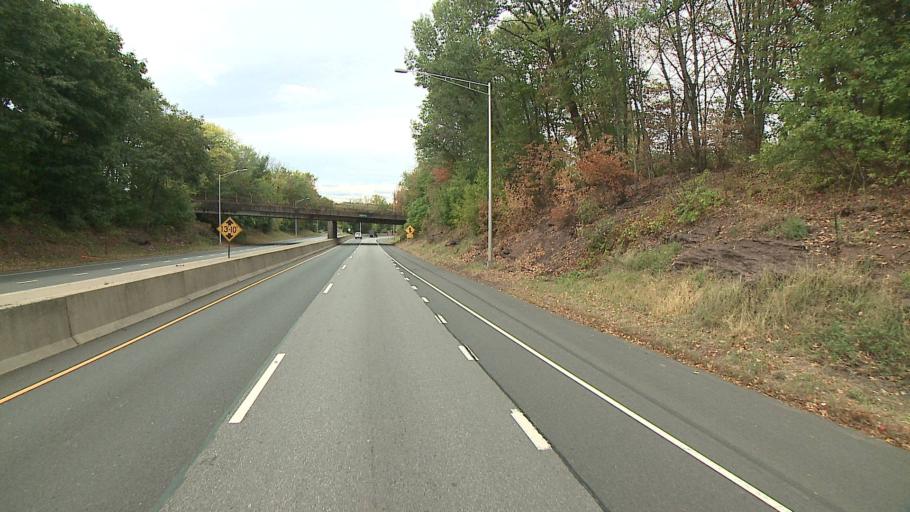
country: US
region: Connecticut
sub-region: Middlesex County
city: Middletown
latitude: 41.5548
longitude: -72.6376
